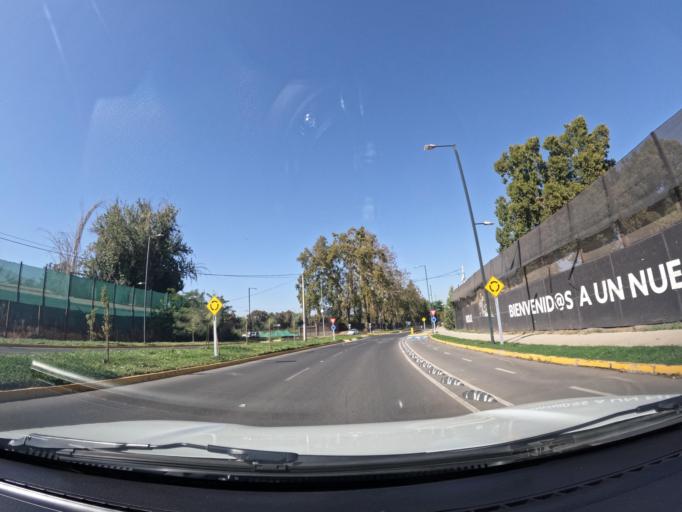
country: CL
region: Santiago Metropolitan
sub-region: Provincia de Santiago
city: Villa Presidente Frei, Nunoa, Santiago, Chile
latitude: -33.4886
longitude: -70.5663
